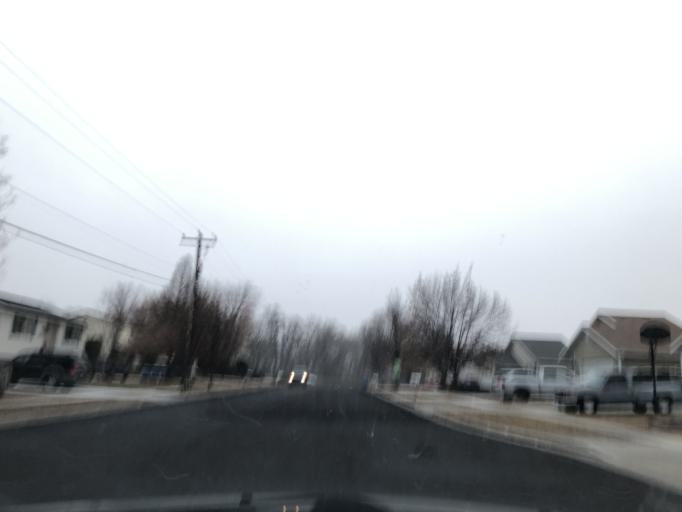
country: US
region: Utah
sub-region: Cache County
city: Logan
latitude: 41.7167
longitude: -111.8426
